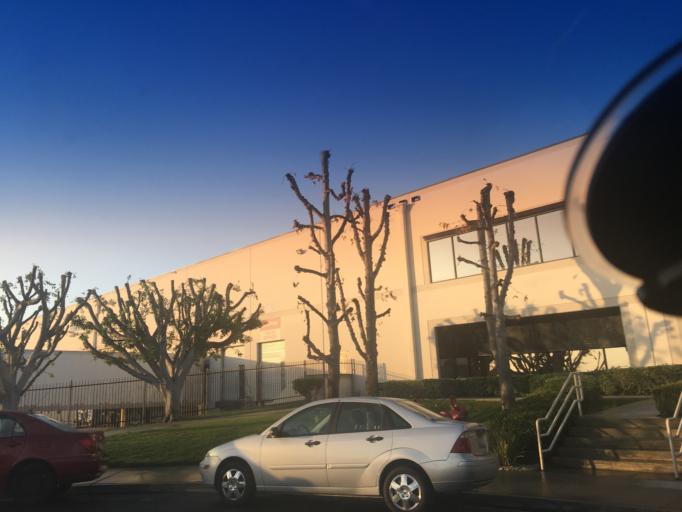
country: US
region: California
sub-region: Orange County
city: Anaheim
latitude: 33.8233
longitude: -117.9008
